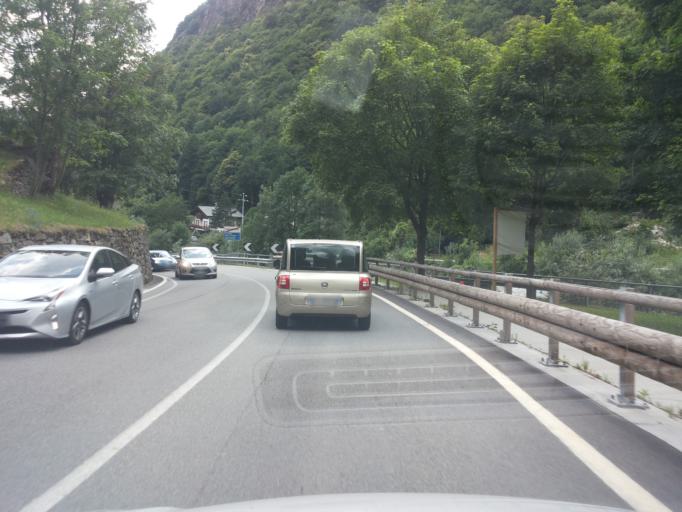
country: IT
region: Aosta Valley
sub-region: Valle d'Aosta
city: Fontainemore
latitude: 45.6456
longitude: 7.8582
